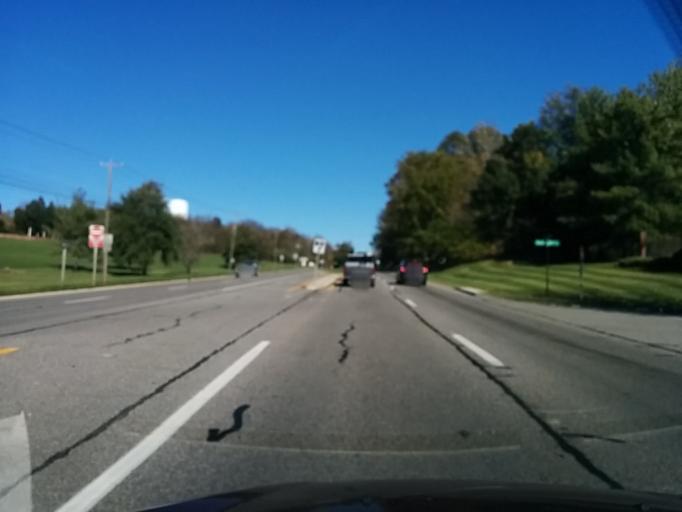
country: US
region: Virginia
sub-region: Roanoke County
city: Hollins
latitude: 37.3527
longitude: -79.9376
